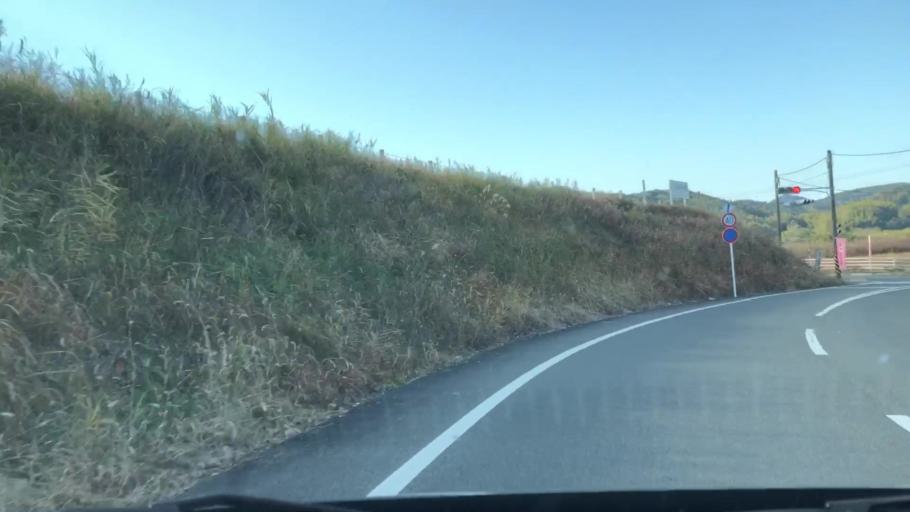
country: JP
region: Kagoshima
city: Satsumasendai
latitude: 31.8650
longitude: 130.3295
